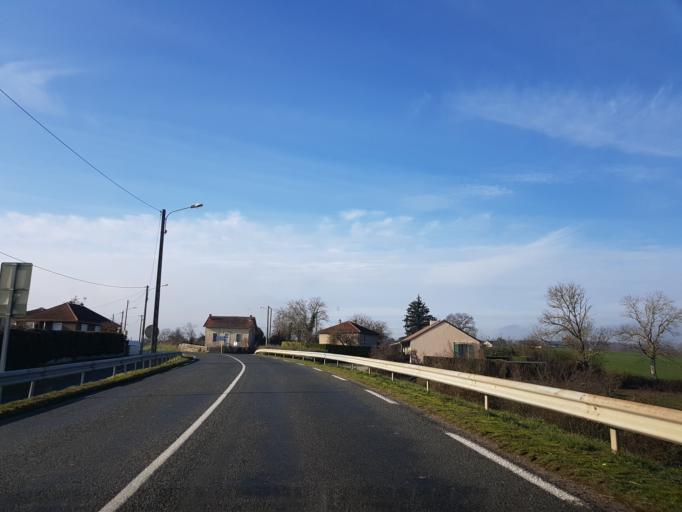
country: FR
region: Bourgogne
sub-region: Departement de Saone-et-Loire
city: Gueugnon
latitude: 46.5959
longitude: 4.0375
